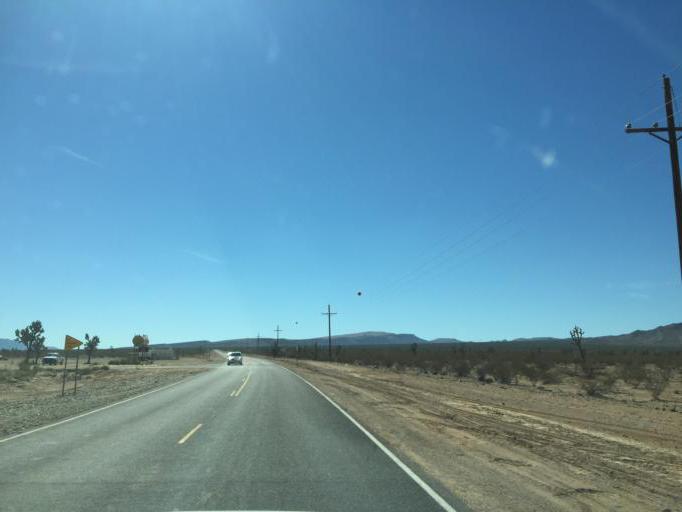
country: US
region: Arizona
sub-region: Mohave County
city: Meadview
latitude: 35.7782
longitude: -114.1327
